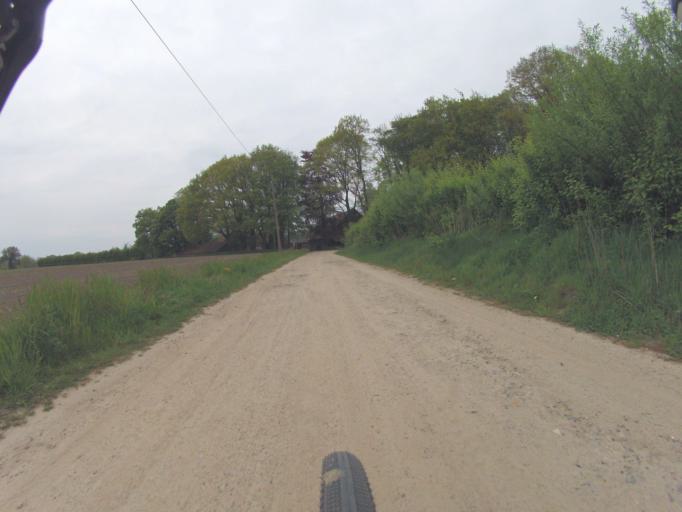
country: DE
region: North Rhine-Westphalia
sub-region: Regierungsbezirk Munster
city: Westerkappeln
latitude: 52.3146
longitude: 7.8367
